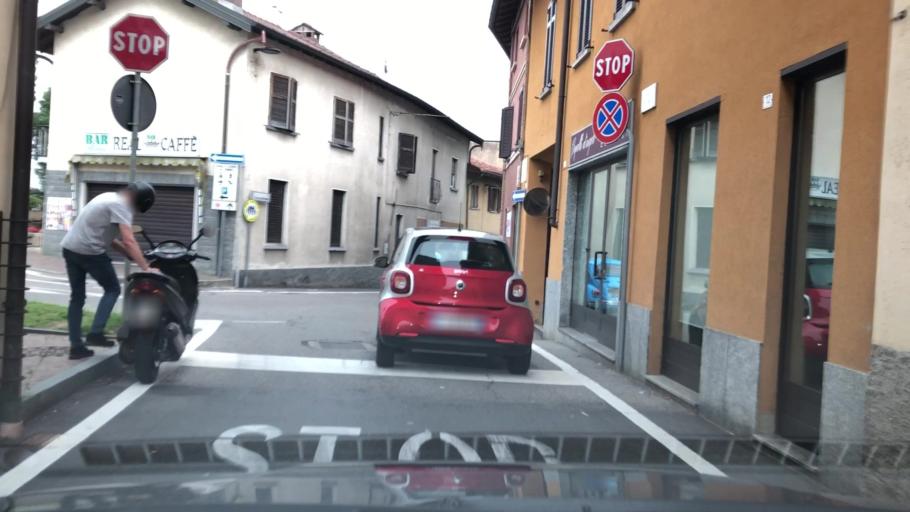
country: IT
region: Lombardy
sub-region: Provincia di Como
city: Casnate Con Bernate
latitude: 45.7570
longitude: 9.0737
